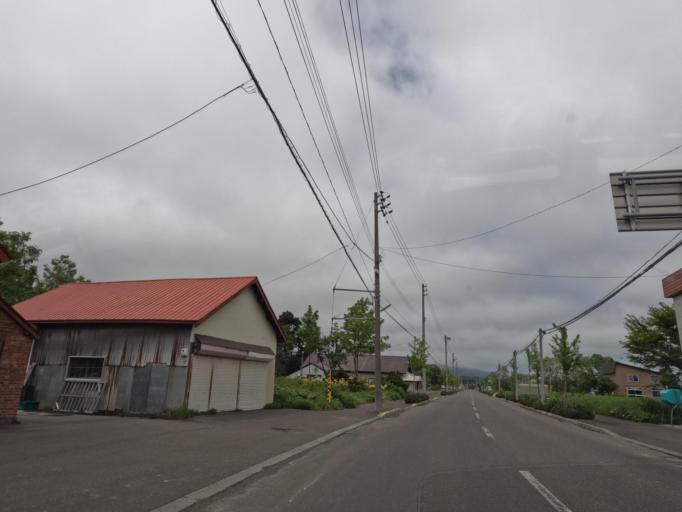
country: JP
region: Hokkaido
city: Tobetsu
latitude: 43.2380
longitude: 141.5131
